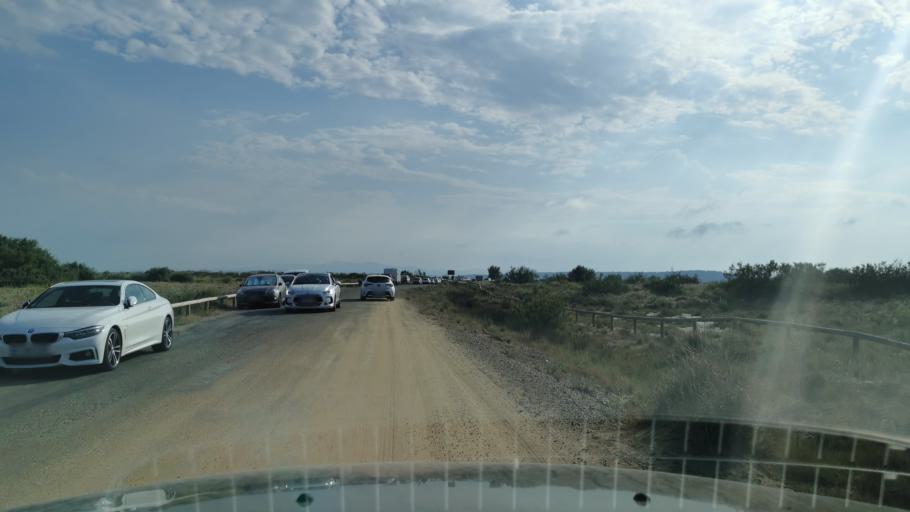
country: FR
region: Languedoc-Roussillon
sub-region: Departement de l'Aude
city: Gruissan
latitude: 43.1149
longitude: 3.1270
